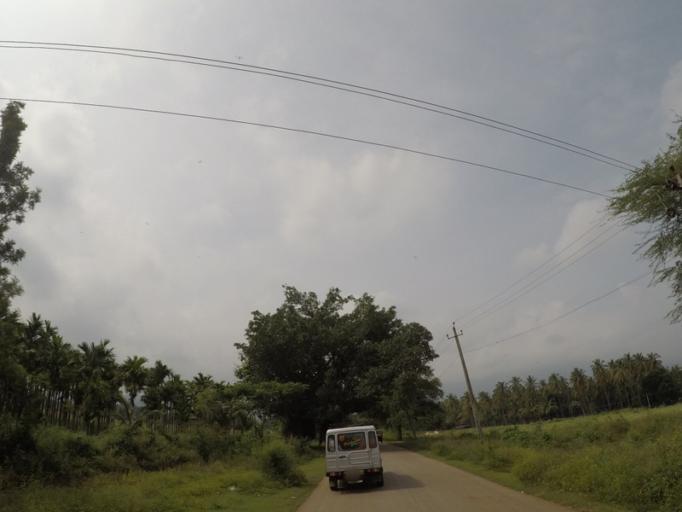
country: IN
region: Karnataka
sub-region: Chikmagalur
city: Tarikere
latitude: 13.5785
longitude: 75.8229
